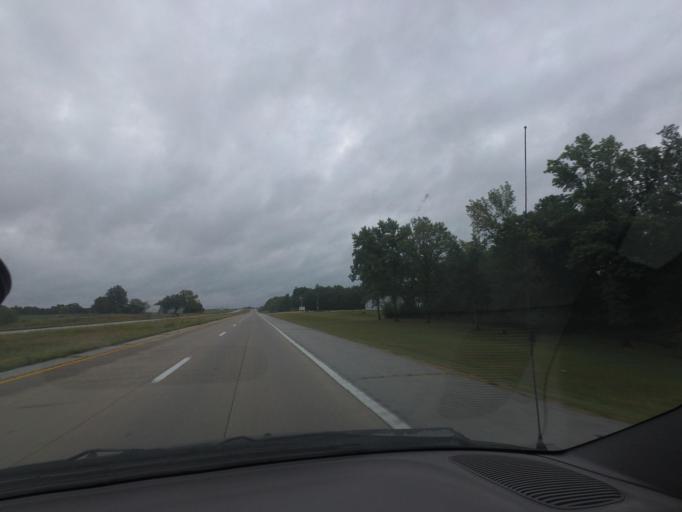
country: US
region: Missouri
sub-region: Marion County
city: Monroe City
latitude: 39.6736
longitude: -91.8793
